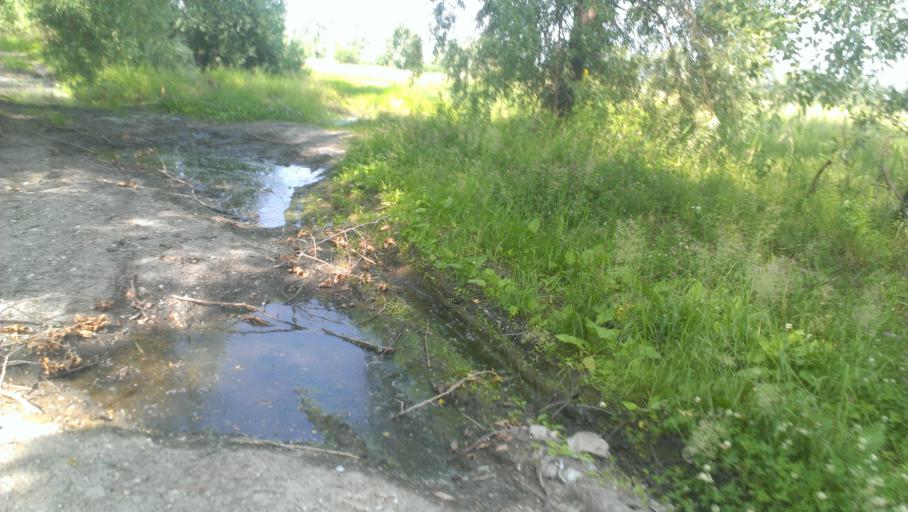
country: RU
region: Altai Krai
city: Novoaltaysk
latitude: 53.3758
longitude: 83.8569
